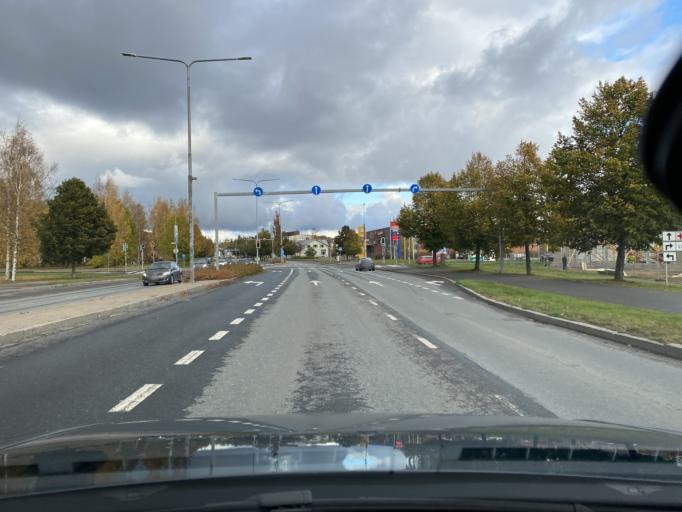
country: FI
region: Haeme
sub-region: Forssa
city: Forssa
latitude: 60.8111
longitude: 23.6312
